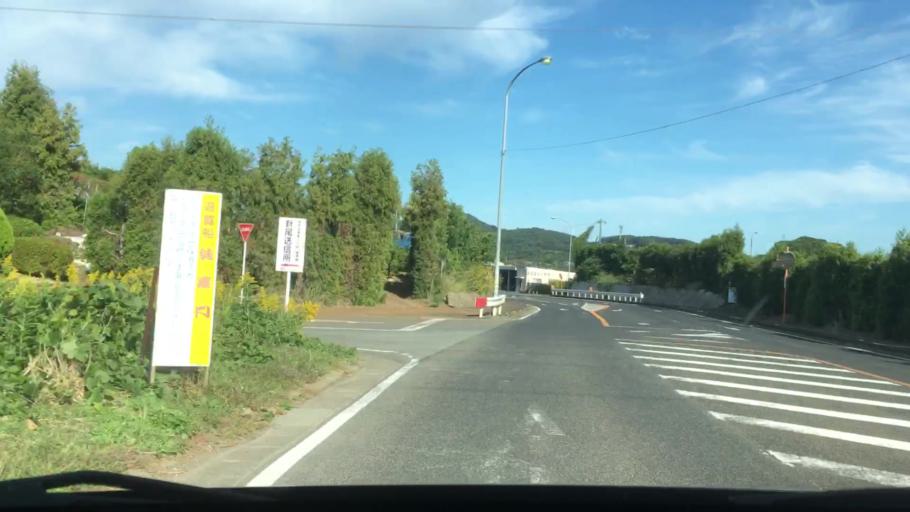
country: JP
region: Nagasaki
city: Sasebo
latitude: 33.0750
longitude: 129.7599
